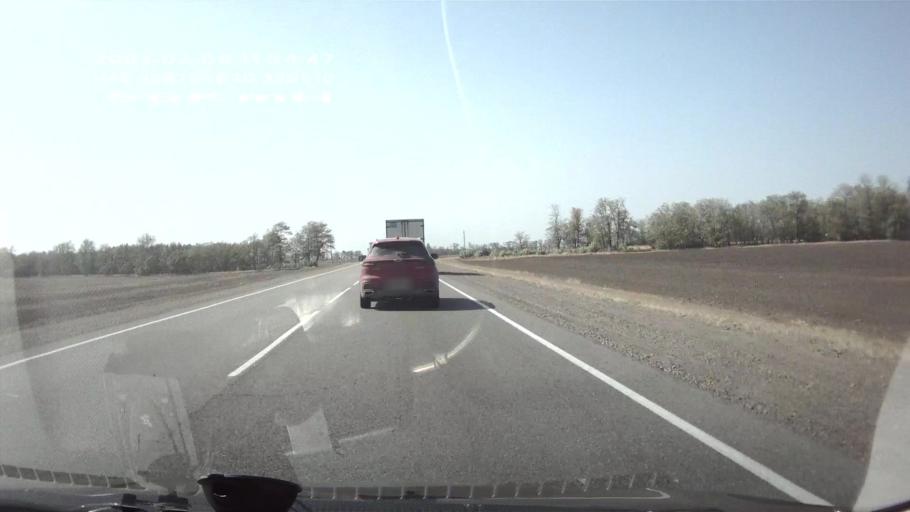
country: RU
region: Krasnodarskiy
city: Kazanskaya
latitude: 45.4389
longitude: 40.3387
